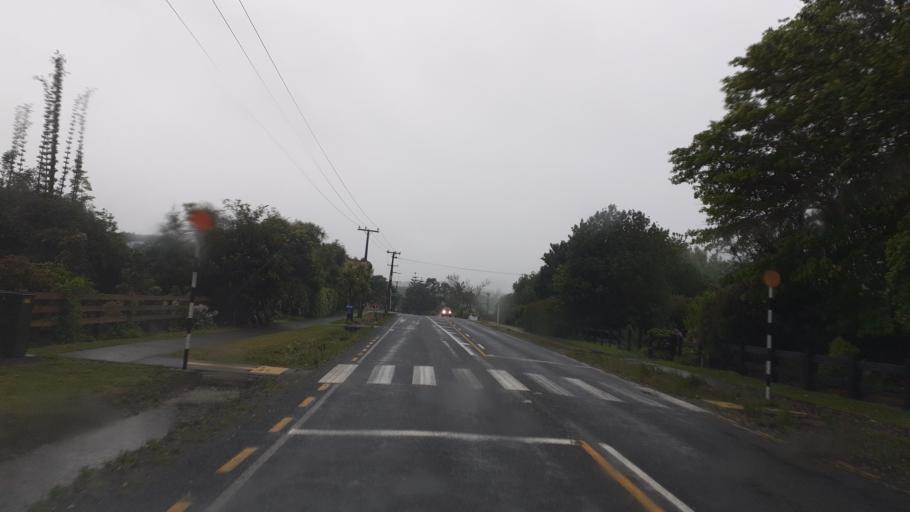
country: NZ
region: Northland
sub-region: Far North District
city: Kerikeri
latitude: -35.2076
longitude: 173.9647
